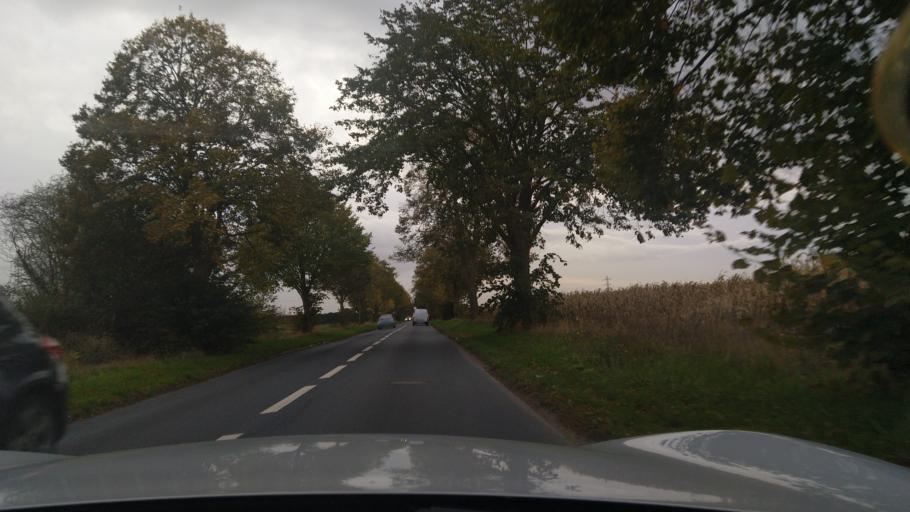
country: FR
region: Ile-de-France
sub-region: Departement de Seine-Saint-Denis
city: Villepinte
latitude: 48.9758
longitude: 2.5569
